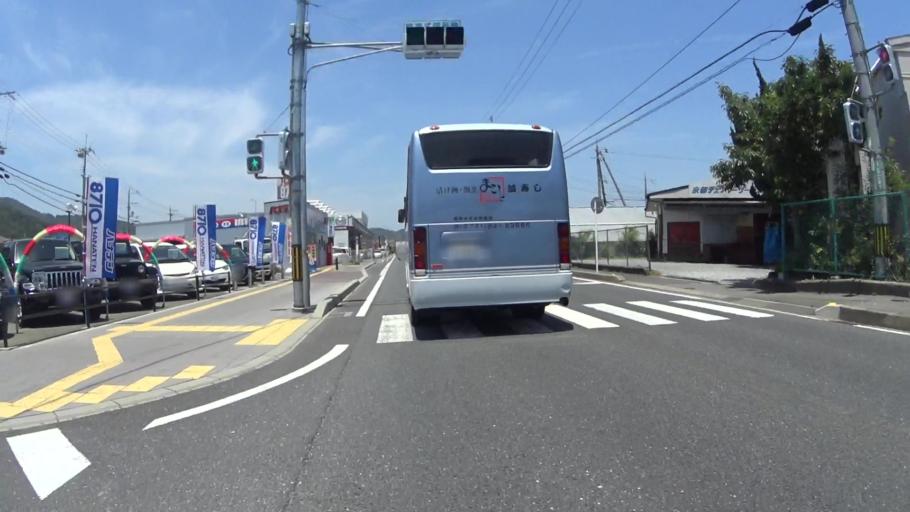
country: JP
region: Kyoto
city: Fukuchiyama
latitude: 35.2782
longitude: 135.1820
